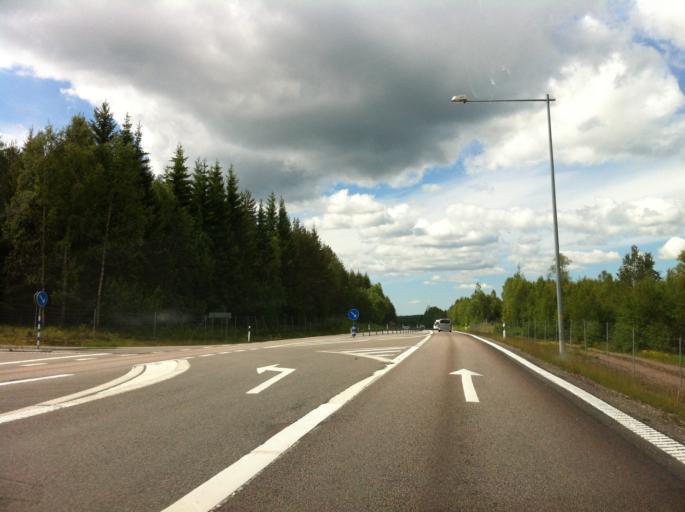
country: SE
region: Vaermland
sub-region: Saffle Kommun
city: Saeffle
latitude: 59.1144
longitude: 12.8227
